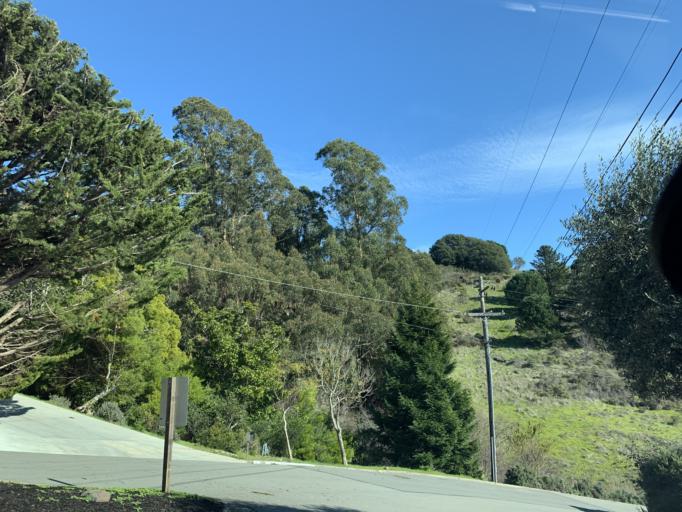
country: US
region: California
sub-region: Marin County
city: Strawberry
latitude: 37.9035
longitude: -122.5110
